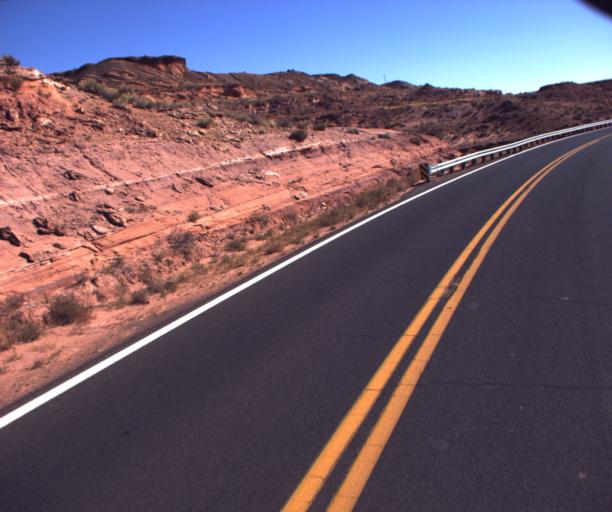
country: US
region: Arizona
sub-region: Coconino County
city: Tuba City
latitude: 36.1082
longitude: -111.2140
